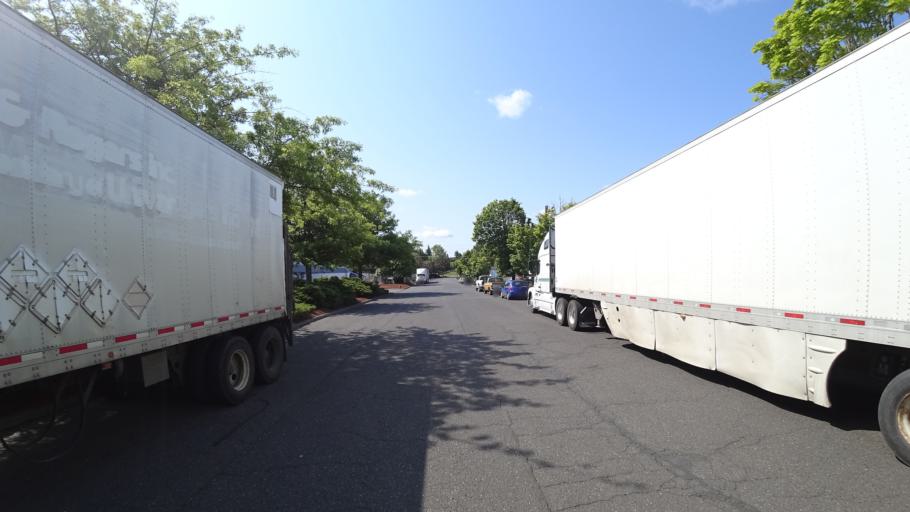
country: US
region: Washington
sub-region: Clark County
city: Vancouver
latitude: 45.6005
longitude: -122.7389
